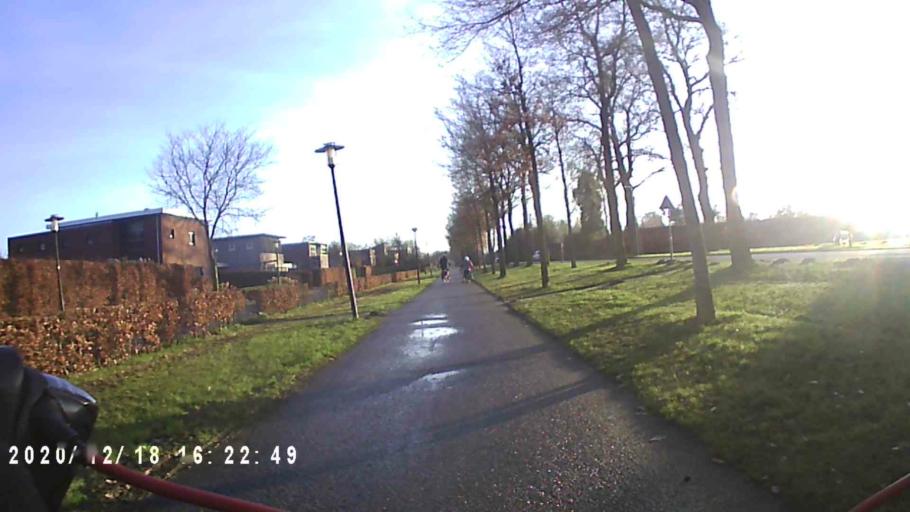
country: NL
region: Drenthe
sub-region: Gemeente Tynaarlo
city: Zuidlaren
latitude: 53.0911
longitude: 6.6912
